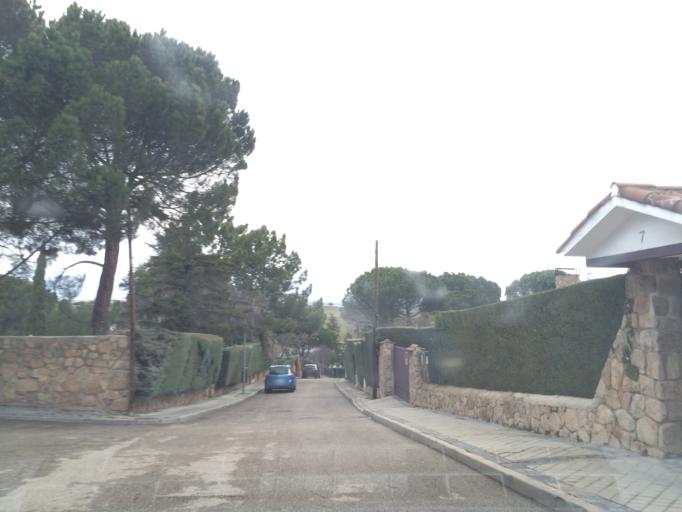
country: ES
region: Madrid
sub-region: Provincia de Madrid
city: Tres Cantos
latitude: 40.6110
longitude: -3.6861
